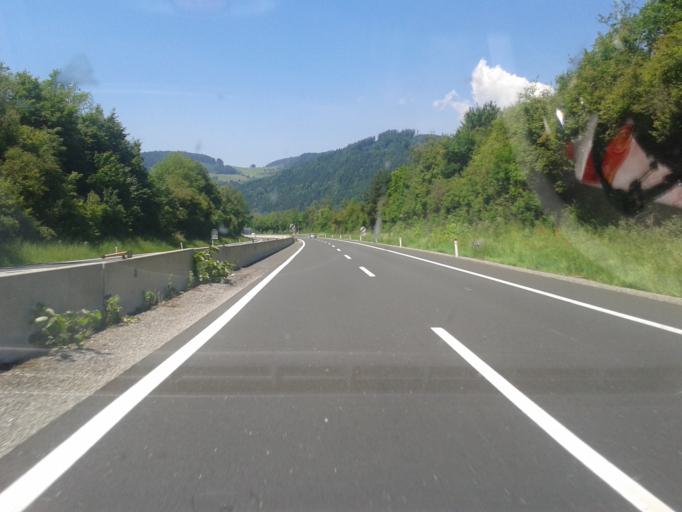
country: AT
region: Carinthia
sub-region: Politischer Bezirk Volkermarkt
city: Griffen
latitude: 46.6962
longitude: 14.7315
